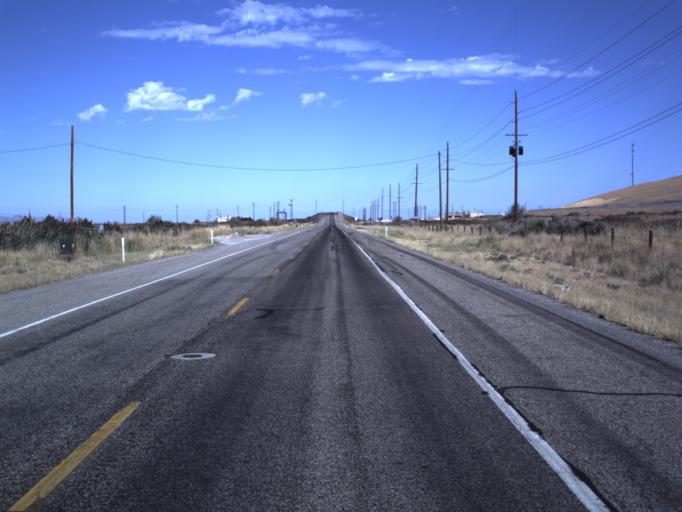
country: US
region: Utah
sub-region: Salt Lake County
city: Magna
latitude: 40.7349
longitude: -112.1710
